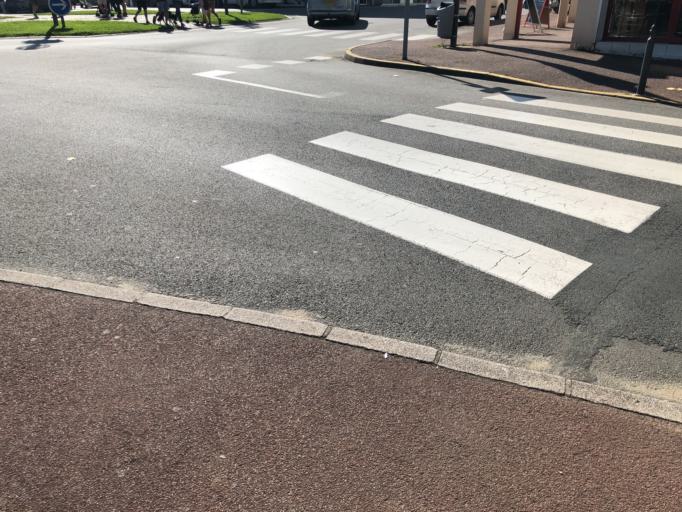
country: FR
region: Pays de la Loire
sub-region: Departement de la Loire-Atlantique
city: Saint-Brevin-les-Pins
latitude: 47.2471
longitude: -2.1670
